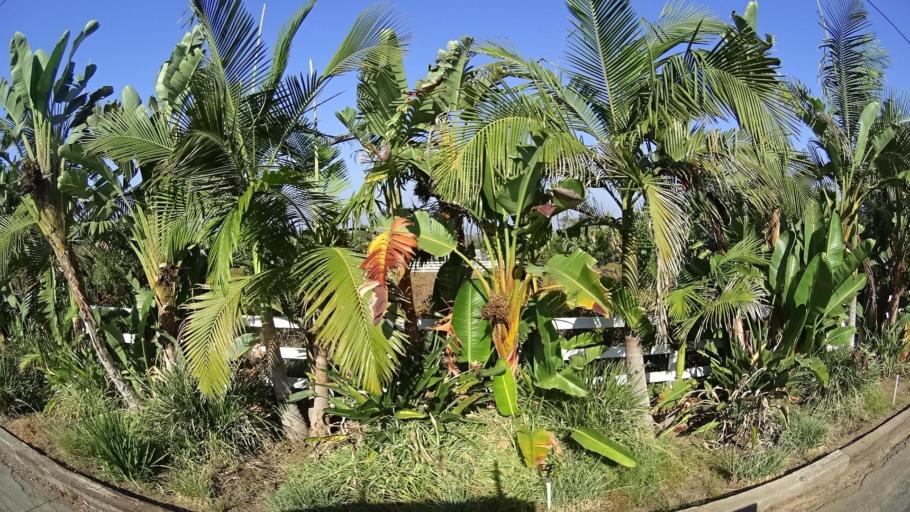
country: US
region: California
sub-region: San Diego County
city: Fallbrook
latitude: 33.3277
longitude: -117.2558
